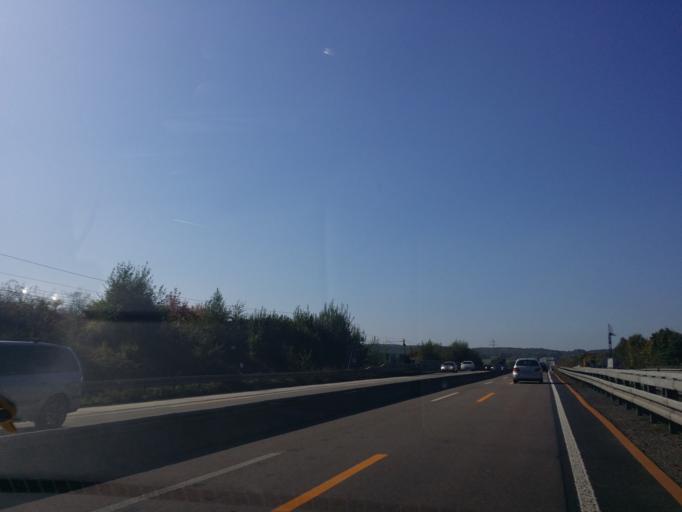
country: DE
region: Hesse
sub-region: Regierungsbezirk Giessen
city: Elz
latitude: 50.4038
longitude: 8.0441
